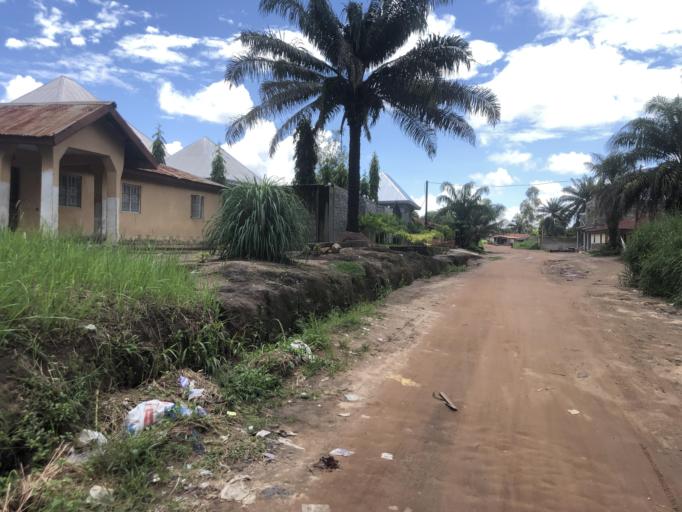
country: SL
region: Northern Province
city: Makeni
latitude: 8.8606
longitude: -12.0485
